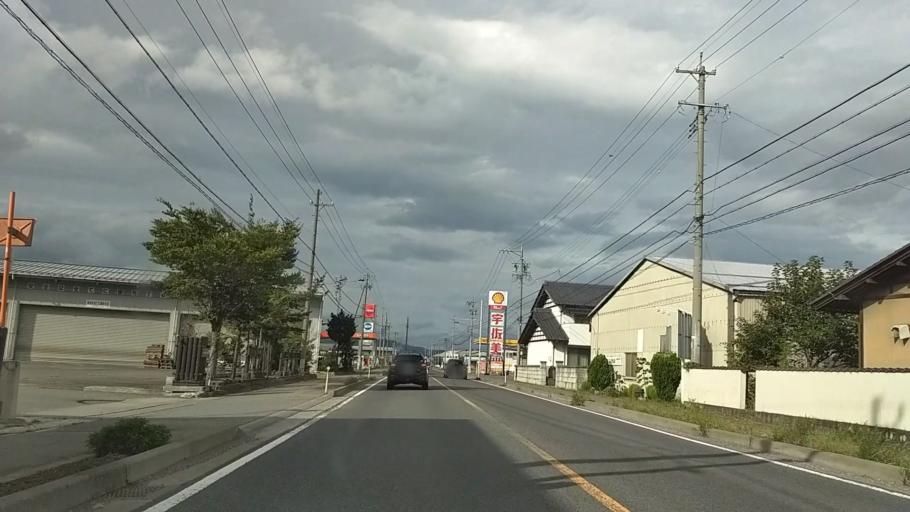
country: JP
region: Nagano
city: Suzaka
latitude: 36.6712
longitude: 138.2654
